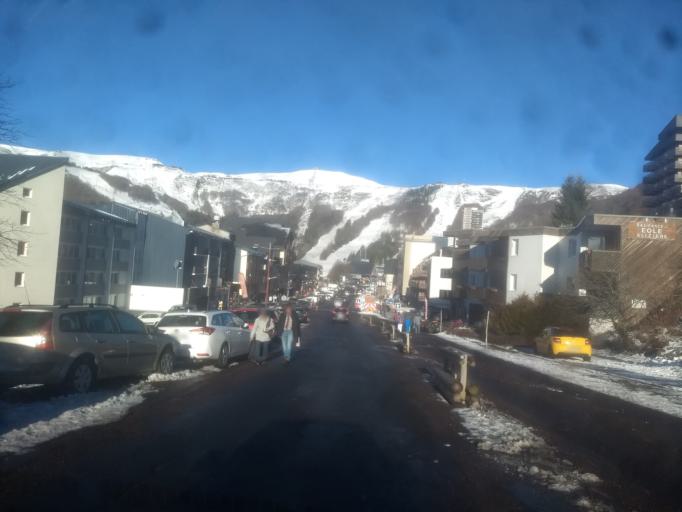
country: FR
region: Auvergne
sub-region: Departement du Puy-de-Dome
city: Mont-Dore
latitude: 45.5104
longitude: 2.8576
